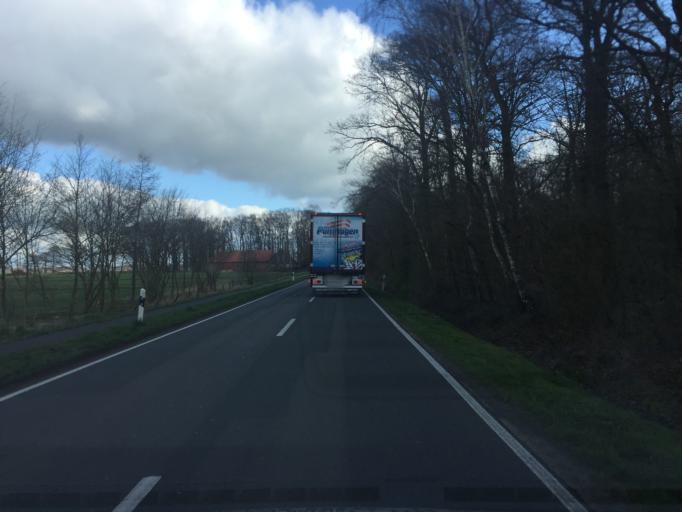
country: DE
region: Lower Saxony
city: Affinghausen
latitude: 52.7699
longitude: 8.8565
